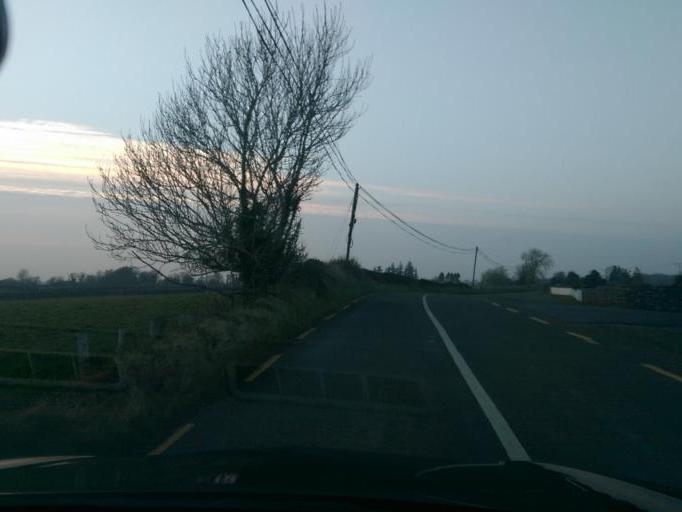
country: IE
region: Connaught
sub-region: County Galway
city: Loughrea
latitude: 53.2197
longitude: -8.6224
